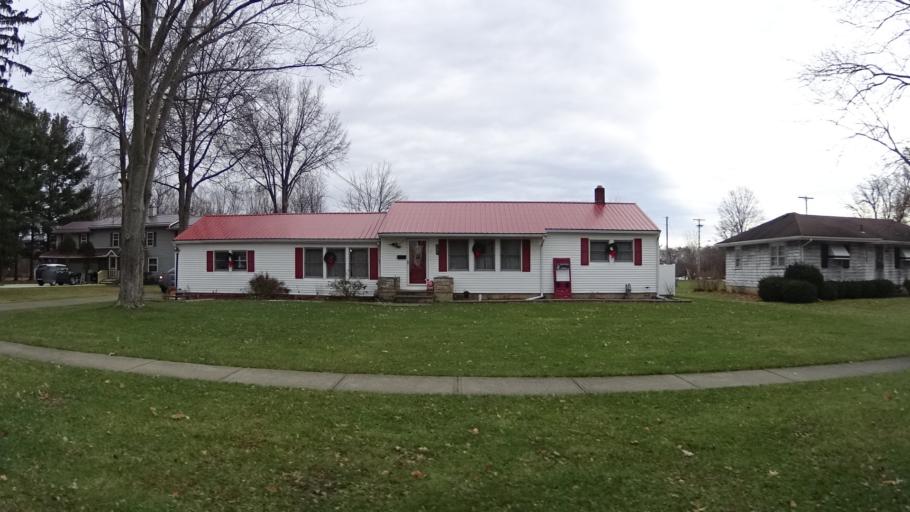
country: US
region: Ohio
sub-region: Lorain County
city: Wellington
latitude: 41.1661
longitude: -82.2102
